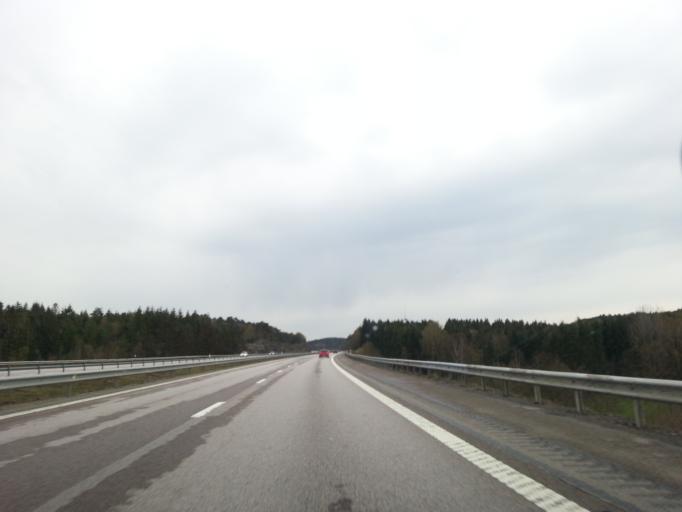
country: SE
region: Halland
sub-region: Kungsbacka Kommun
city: Frillesas
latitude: 57.3496
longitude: 12.2092
